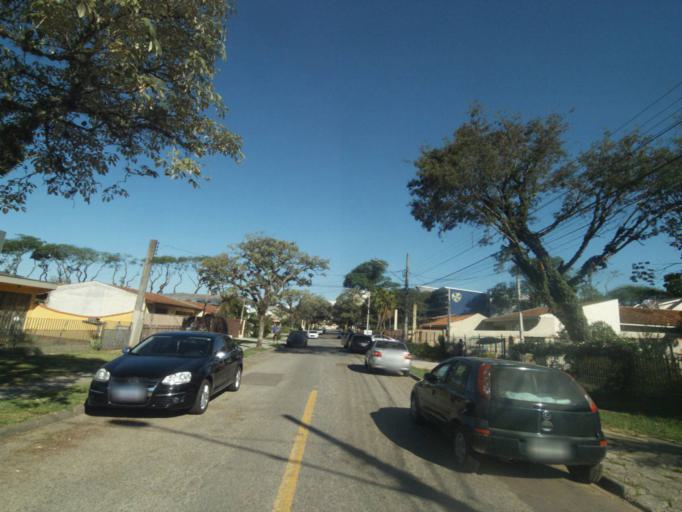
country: BR
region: Parana
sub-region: Curitiba
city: Curitiba
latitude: -25.3900
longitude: -49.2352
